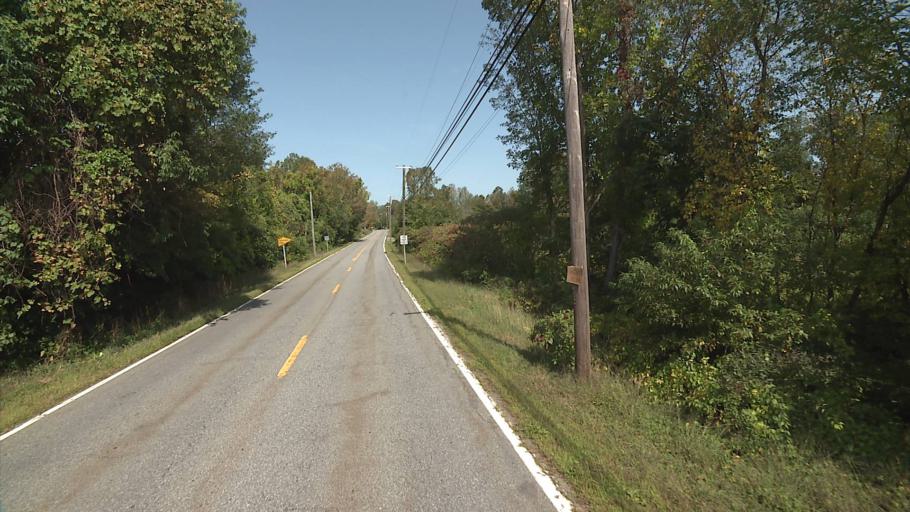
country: US
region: Connecticut
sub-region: Windham County
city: South Woodstock
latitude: 41.9633
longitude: -71.9845
